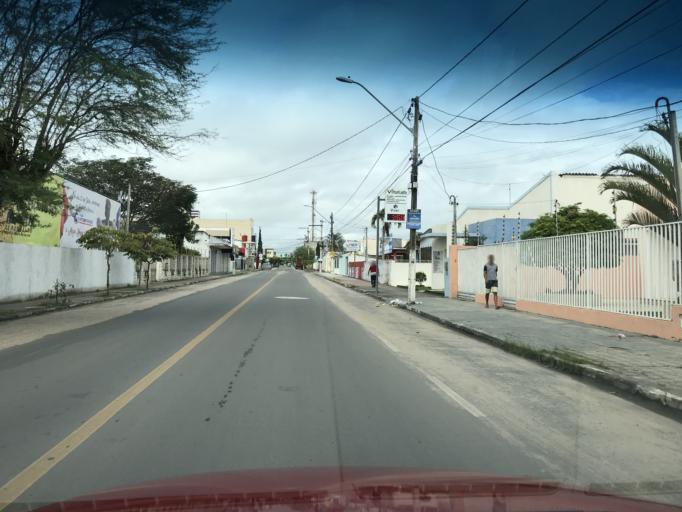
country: BR
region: Bahia
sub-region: Cruz Das Almas
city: Cruz das Almas
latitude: -12.6695
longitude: -39.1020
